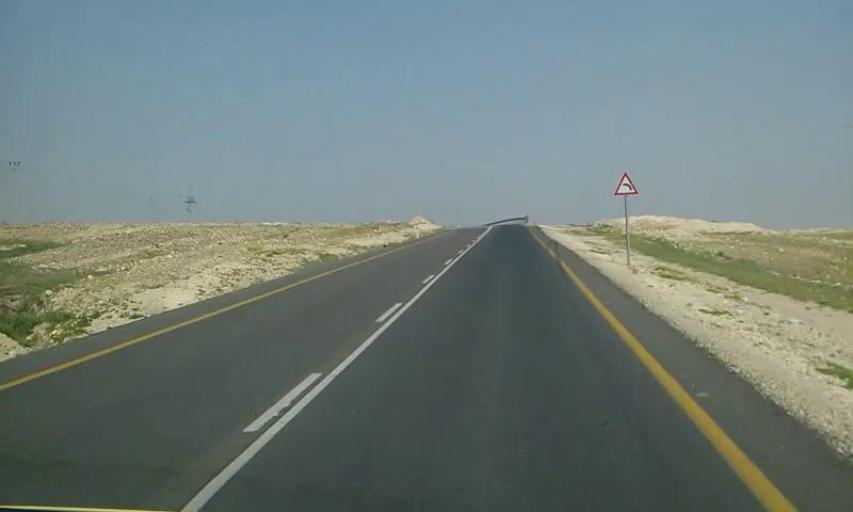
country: PS
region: West Bank
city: Al `Awja
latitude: 31.9704
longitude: 35.4706
